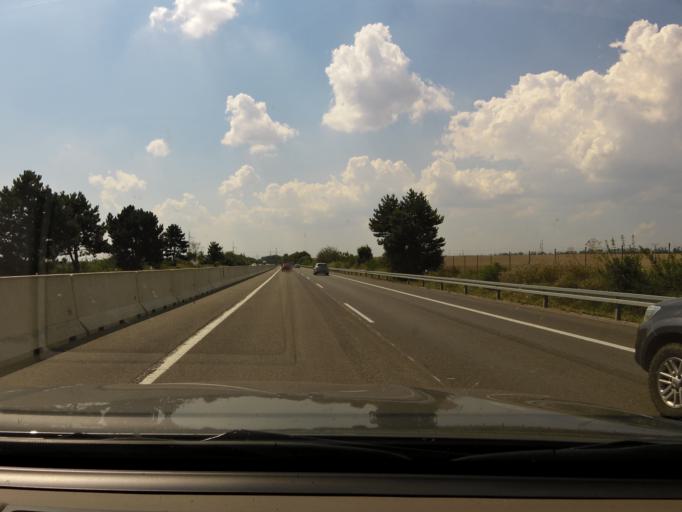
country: SK
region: Trnavsky
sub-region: Okres Trnava
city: Trnava
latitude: 48.3583
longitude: 17.6754
